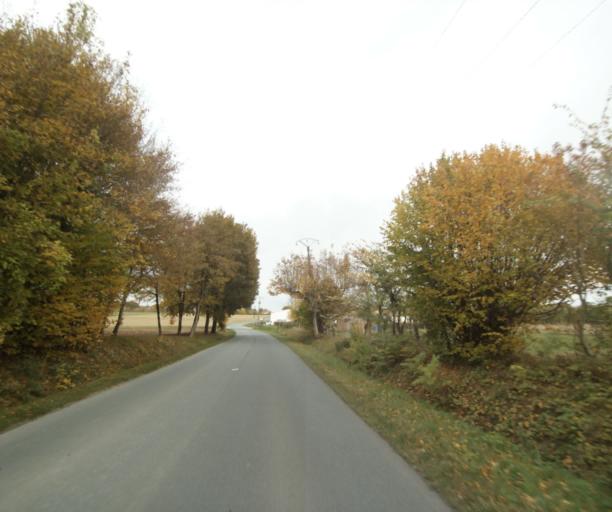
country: FR
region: Poitou-Charentes
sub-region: Departement de la Charente-Maritime
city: Saint-Georges-des-Coteaux
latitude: 45.7717
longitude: -0.7067
